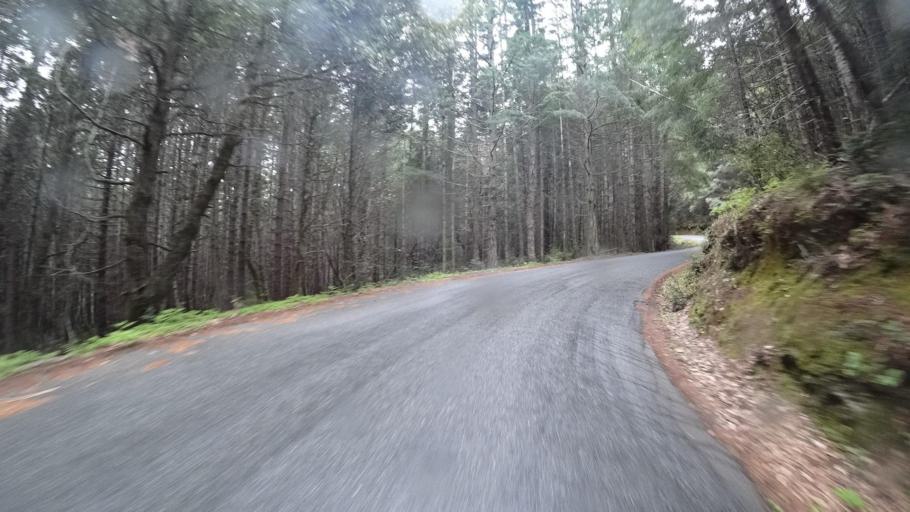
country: US
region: California
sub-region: Humboldt County
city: Willow Creek
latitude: 41.2029
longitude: -123.7759
